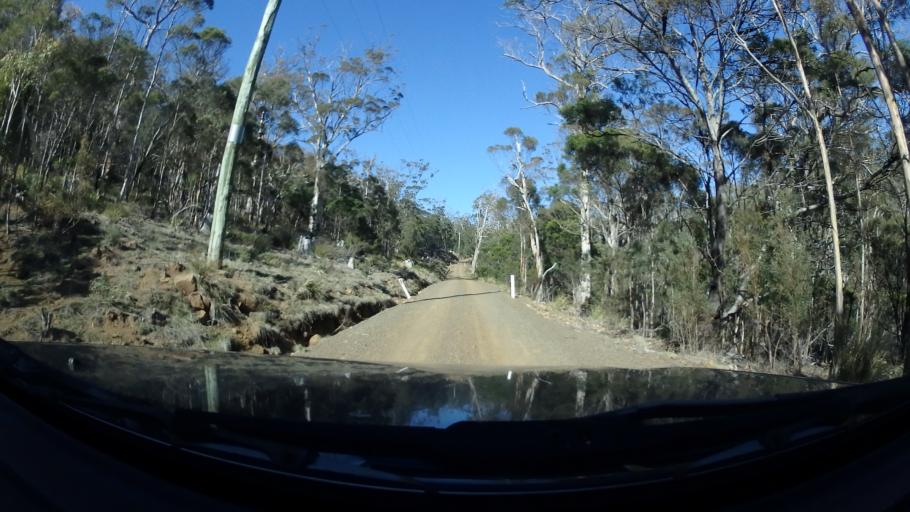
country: AU
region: Tasmania
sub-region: Sorell
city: Sorell
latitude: -42.5400
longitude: 147.8636
